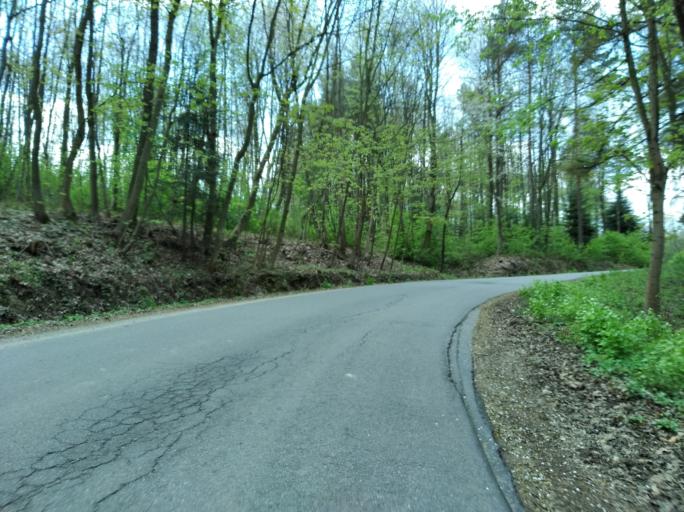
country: PL
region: Subcarpathian Voivodeship
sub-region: Powiat brzozowski
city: Wesola
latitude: 49.7683
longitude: 22.1294
